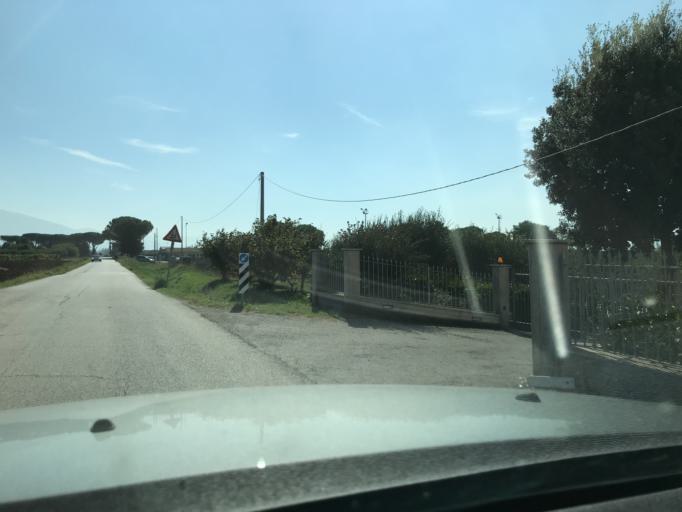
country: IT
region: Umbria
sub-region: Provincia di Perugia
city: Via Lippia
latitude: 43.0957
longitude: 12.4944
